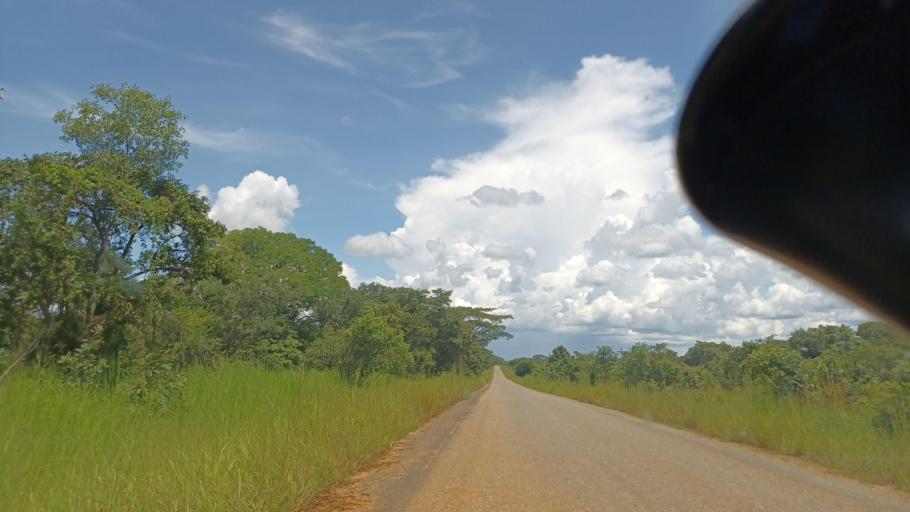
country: ZM
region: North-Western
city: Solwezi
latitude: -12.5980
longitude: 26.1268
